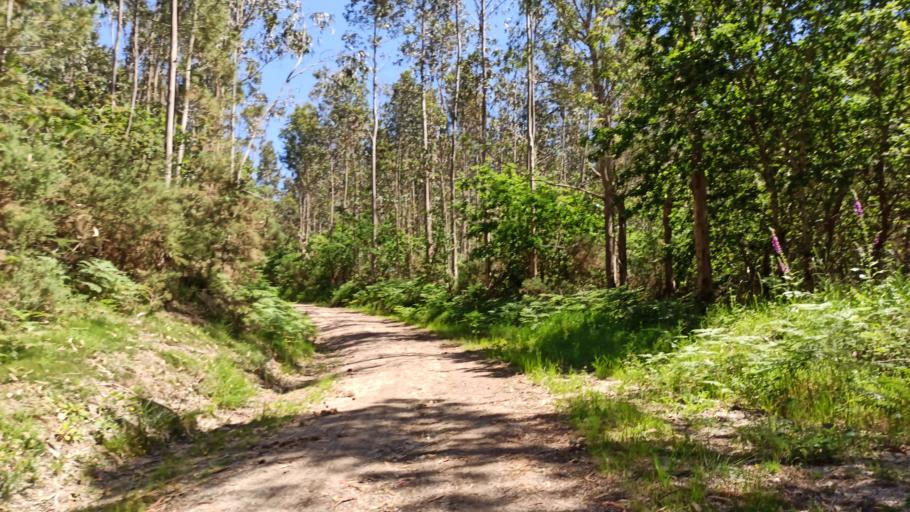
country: ES
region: Galicia
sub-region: Provincia da Coruna
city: Negreira
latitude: 42.9213
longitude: -8.7182
